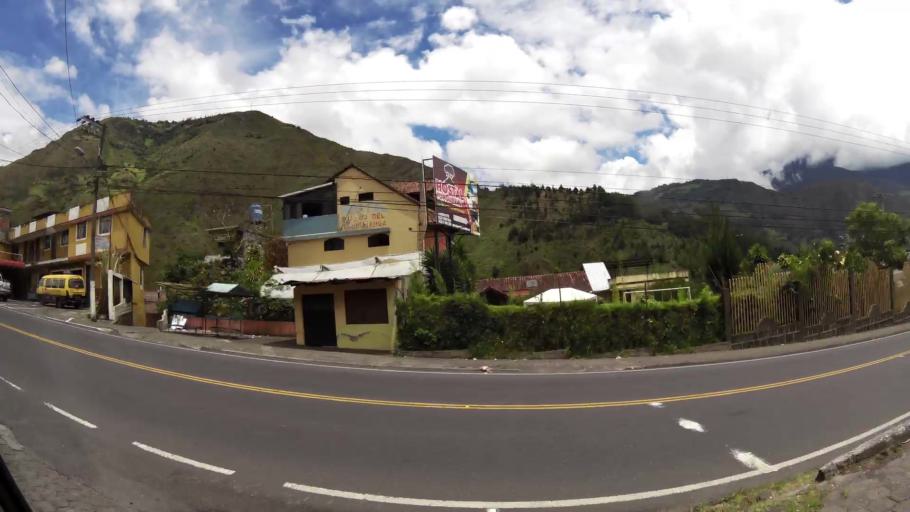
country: EC
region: Tungurahua
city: Banos
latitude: -1.3965
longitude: -78.4295
